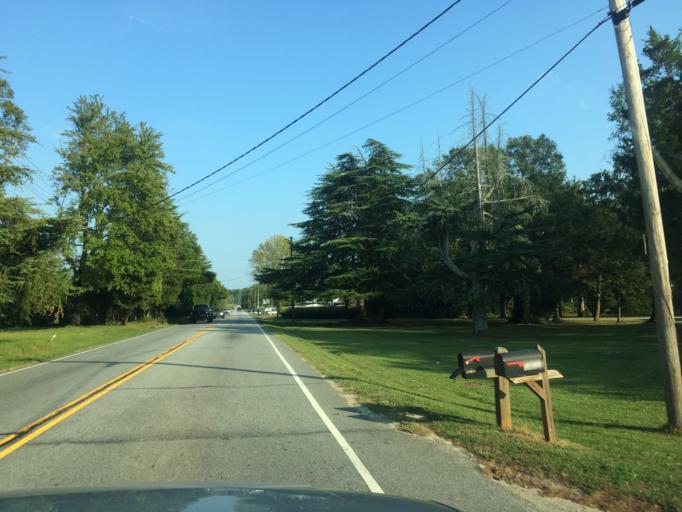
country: US
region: South Carolina
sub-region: Anderson County
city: Piedmont
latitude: 34.7075
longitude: -82.4912
